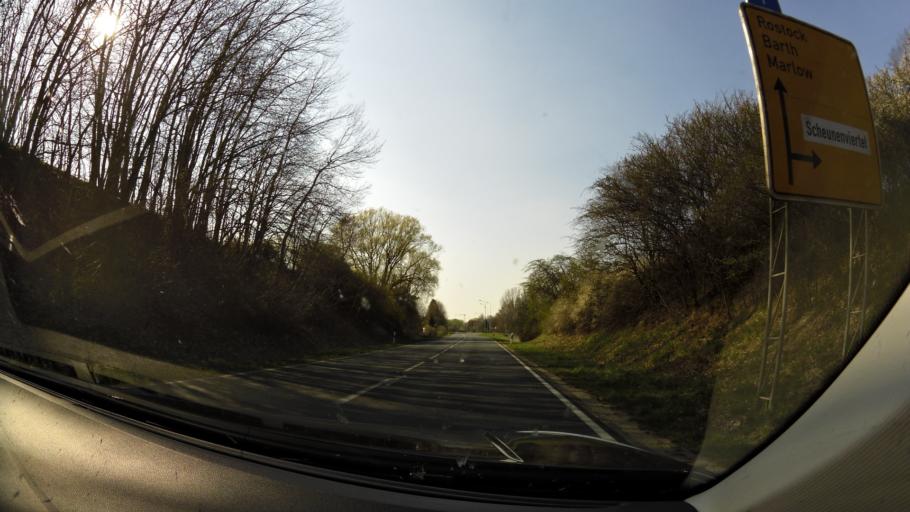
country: DE
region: Mecklenburg-Vorpommern
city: Bad Sulze
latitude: 54.1066
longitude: 12.6585
